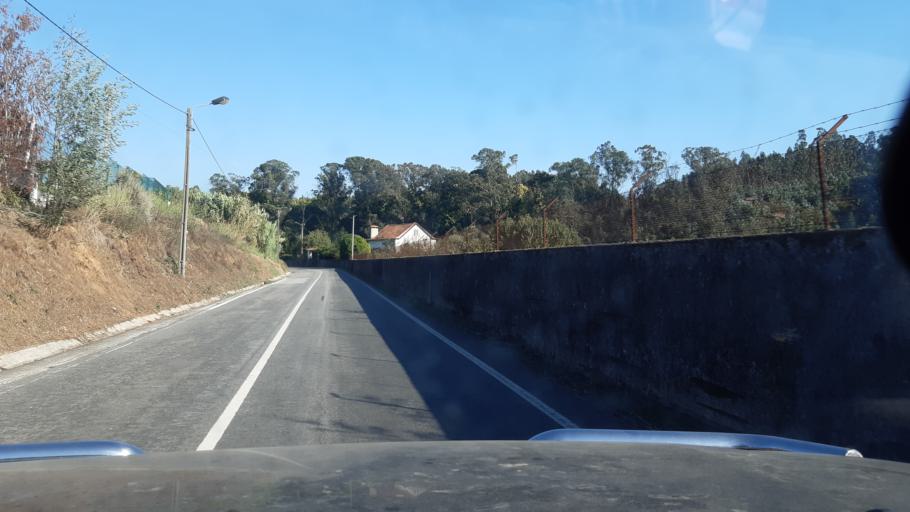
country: PT
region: Aveiro
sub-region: Agueda
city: Agueda
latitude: 40.5619
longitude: -8.4287
